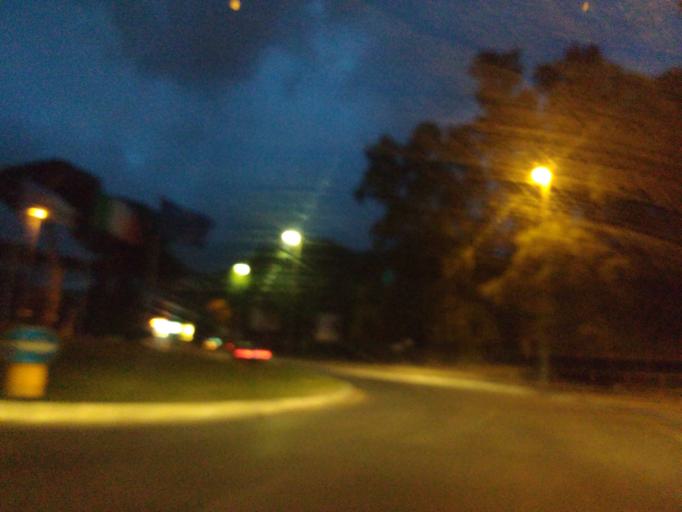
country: IT
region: Latium
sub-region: Citta metropolitana di Roma Capitale
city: Anzio
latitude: 41.4638
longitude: 12.6219
